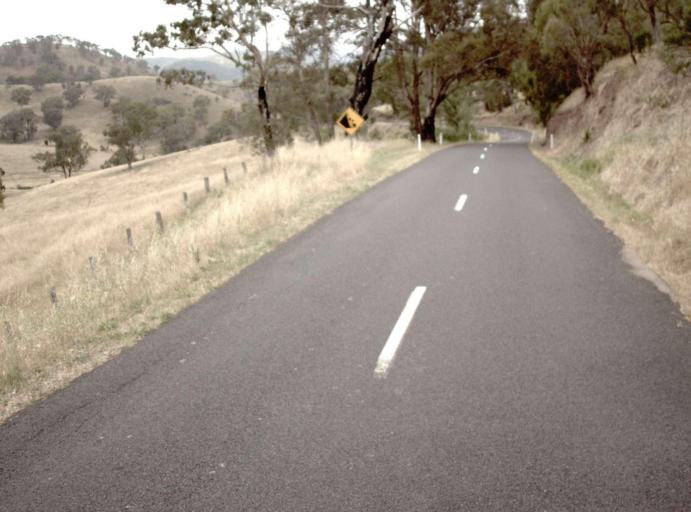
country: AU
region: Victoria
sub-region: Wellington
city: Heyfield
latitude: -37.6862
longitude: 146.6563
